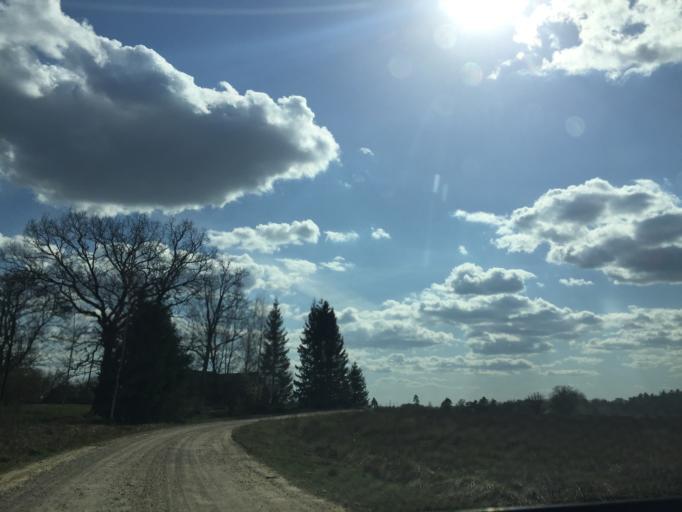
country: LV
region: Skriveri
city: Skriveri
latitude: 56.7752
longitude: 25.1976
